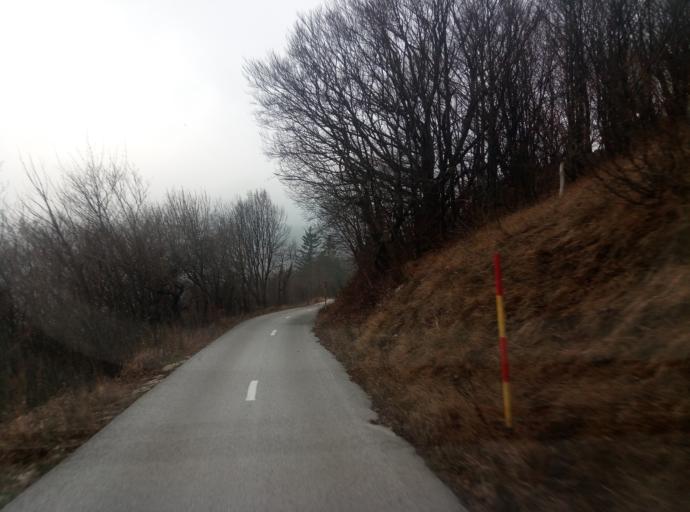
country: SI
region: Vipava
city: Vipava
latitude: 45.9024
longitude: 14.0318
